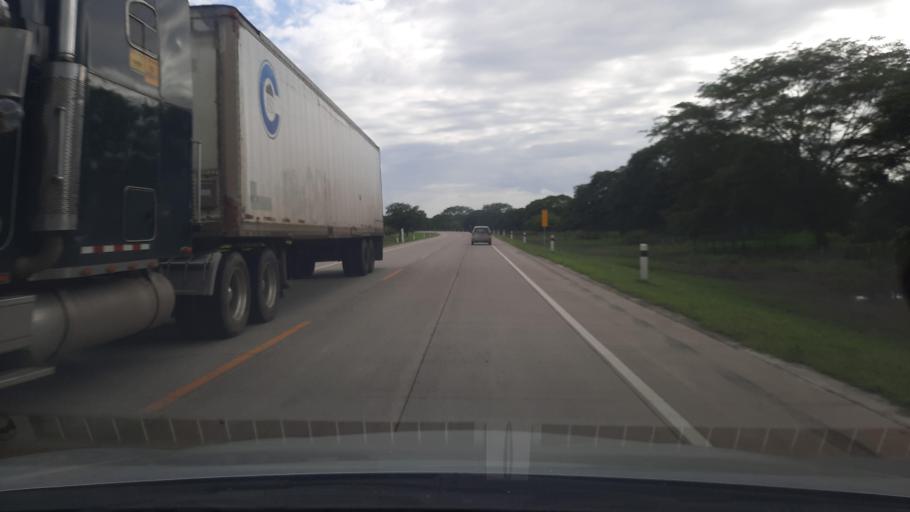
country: NI
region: Chinandega
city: Somotillo
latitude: 12.8376
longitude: -86.8887
